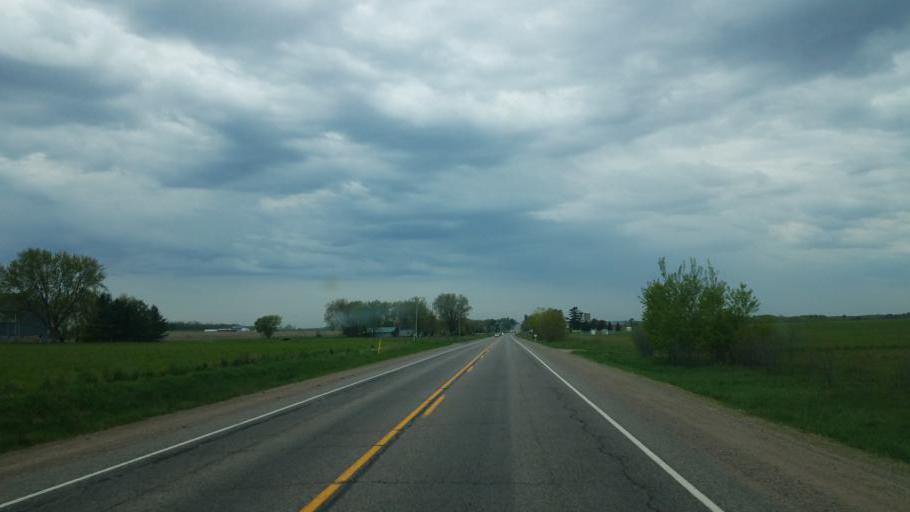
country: US
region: Wisconsin
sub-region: Marathon County
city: Spencer
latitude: 44.5984
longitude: -90.3413
